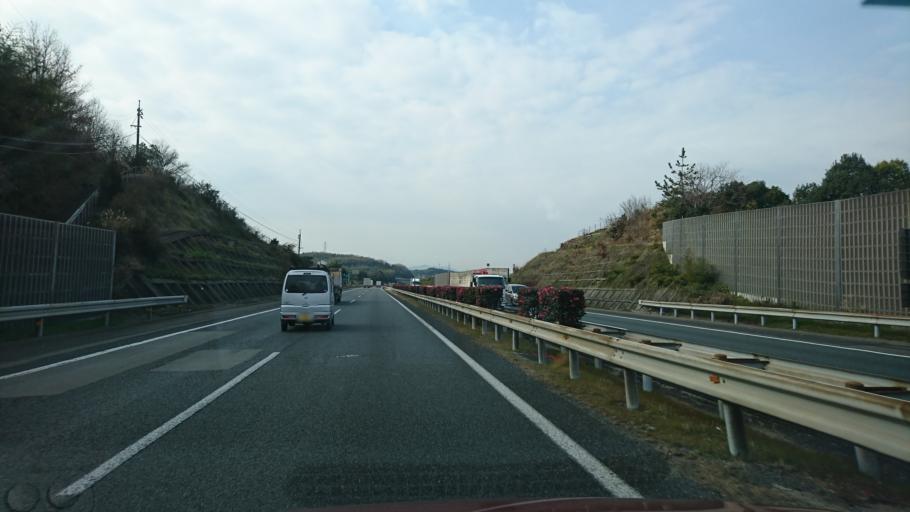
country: JP
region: Hiroshima
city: Kannabecho-yahiro
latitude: 34.5341
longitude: 133.4549
